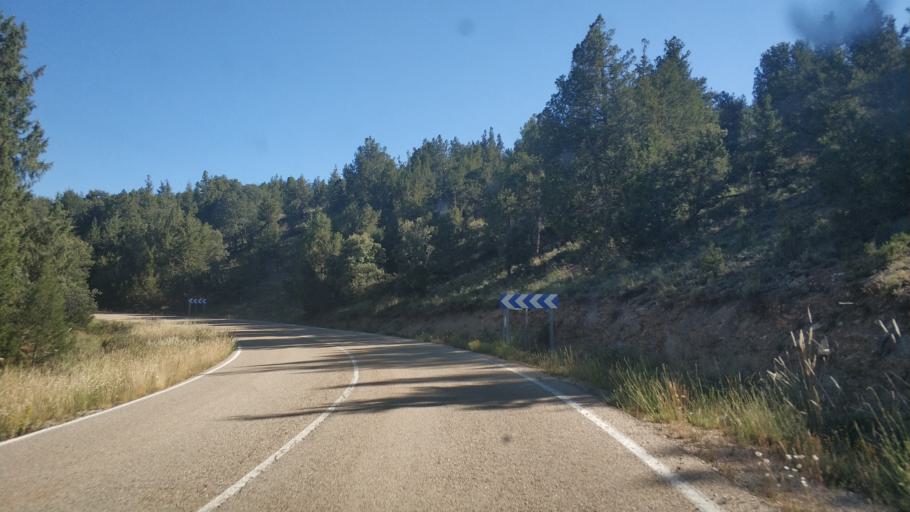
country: ES
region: Castille and Leon
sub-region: Provincia de Soria
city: Montejo de Tiermes
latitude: 41.4306
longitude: -3.2050
